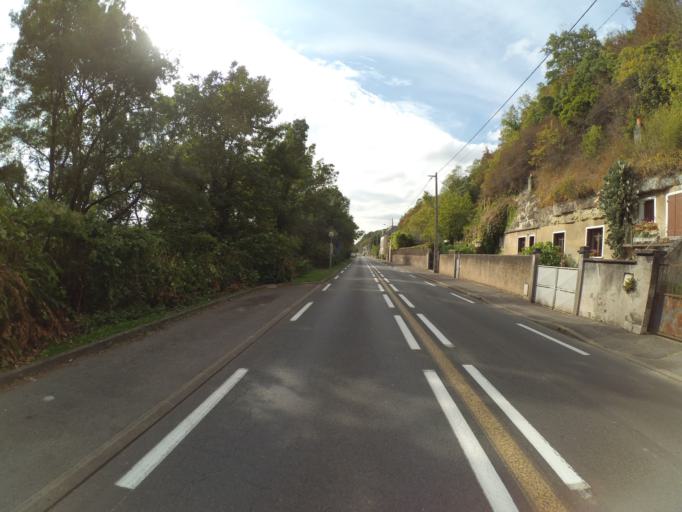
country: FR
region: Centre
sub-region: Departement d'Indre-et-Loire
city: Villandry
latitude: 47.3675
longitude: 0.5101
